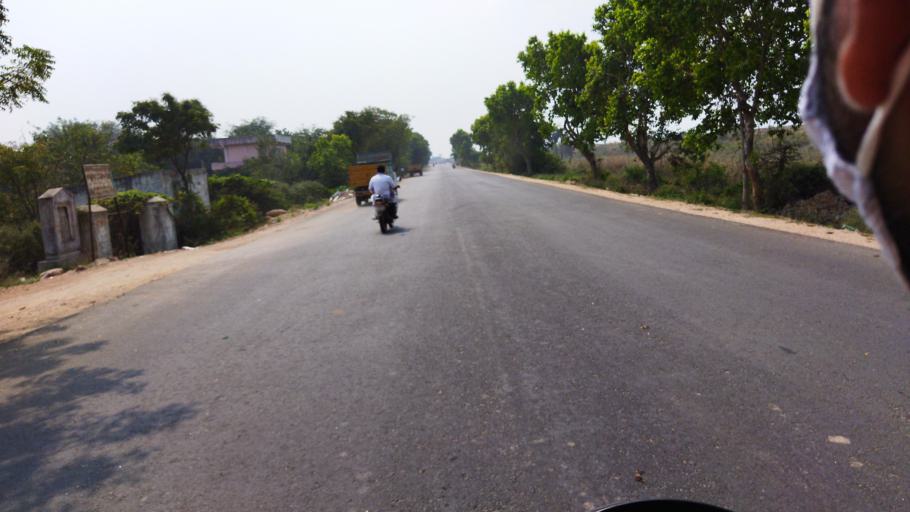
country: IN
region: Telangana
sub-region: Nalgonda
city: Nalgonda
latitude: 17.0818
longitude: 79.3228
